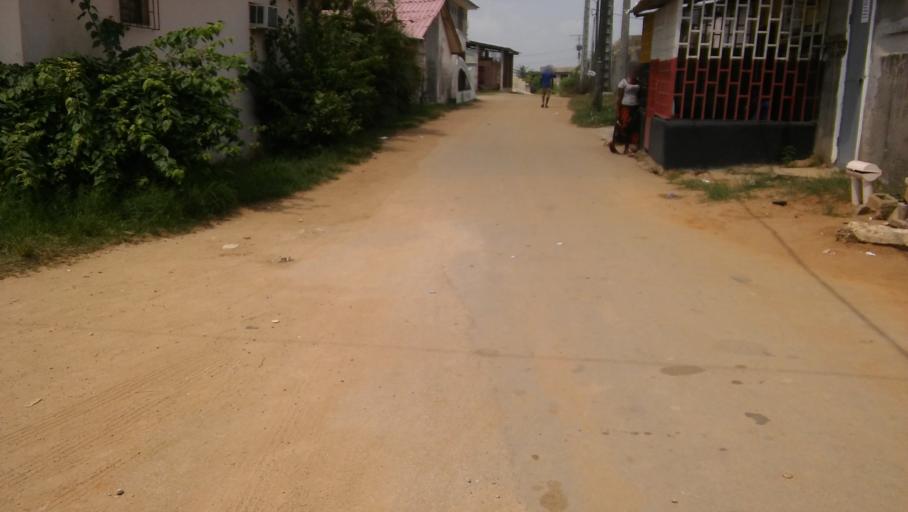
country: CI
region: Sud-Comoe
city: Grand-Bassam
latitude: 5.2180
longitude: -3.7412
